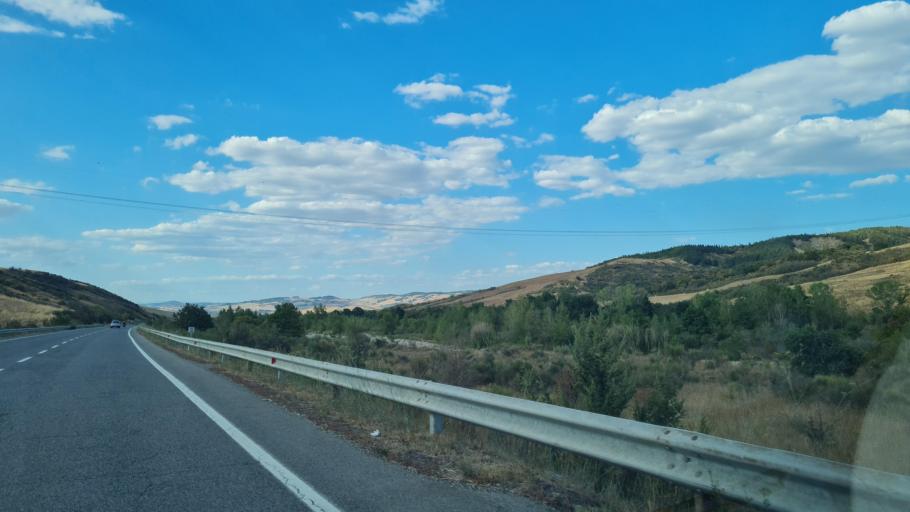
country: IT
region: Tuscany
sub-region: Provincia di Siena
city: Abbadia San Salvatore
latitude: 42.9589
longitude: 11.7063
